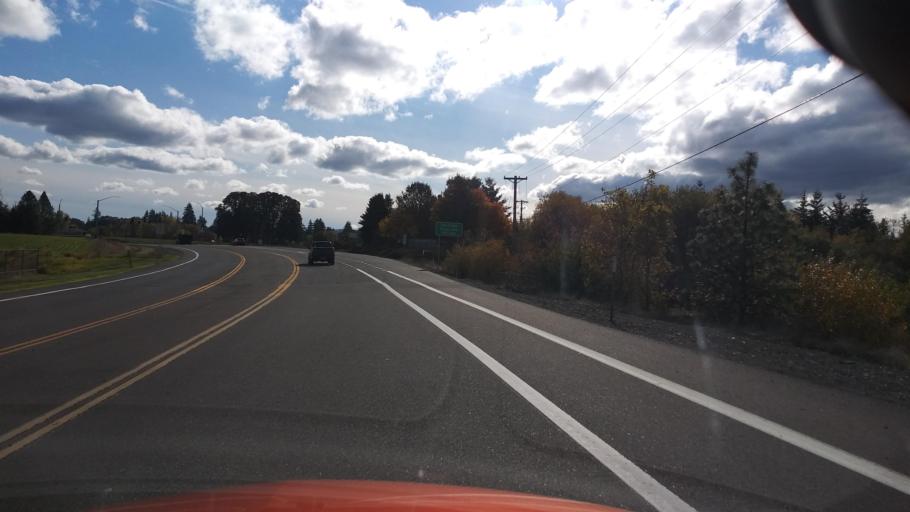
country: US
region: Oregon
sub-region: Washington County
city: Forest Grove
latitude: 45.5372
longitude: -123.1077
